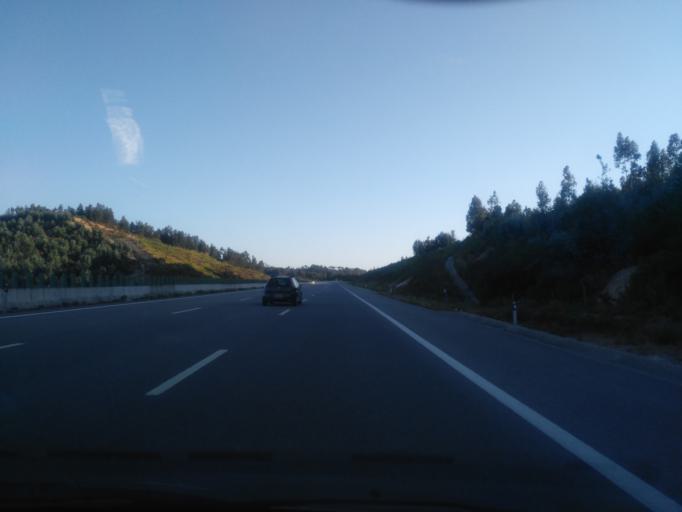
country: PT
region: Coimbra
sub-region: Figueira da Foz
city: Alhadas
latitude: 40.1249
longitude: -8.7466
